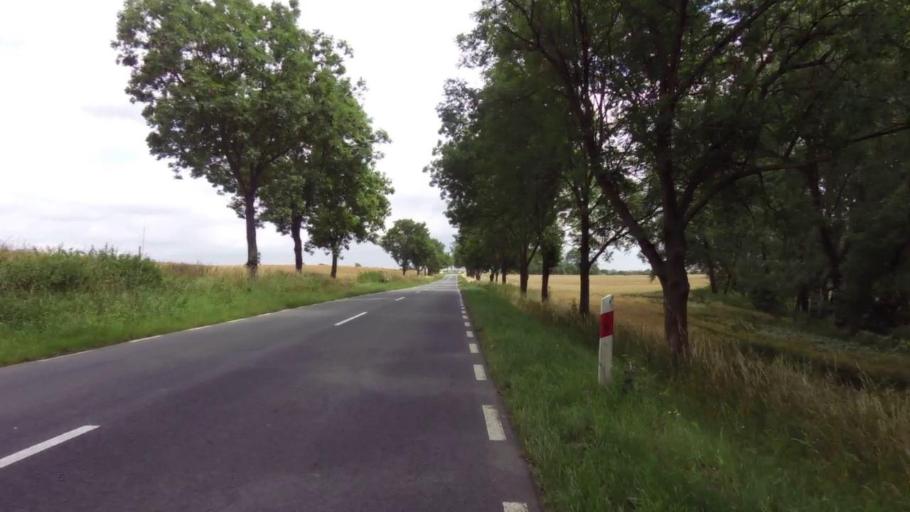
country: PL
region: West Pomeranian Voivodeship
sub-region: Powiat gryfinski
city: Cedynia
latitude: 52.8649
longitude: 14.2798
